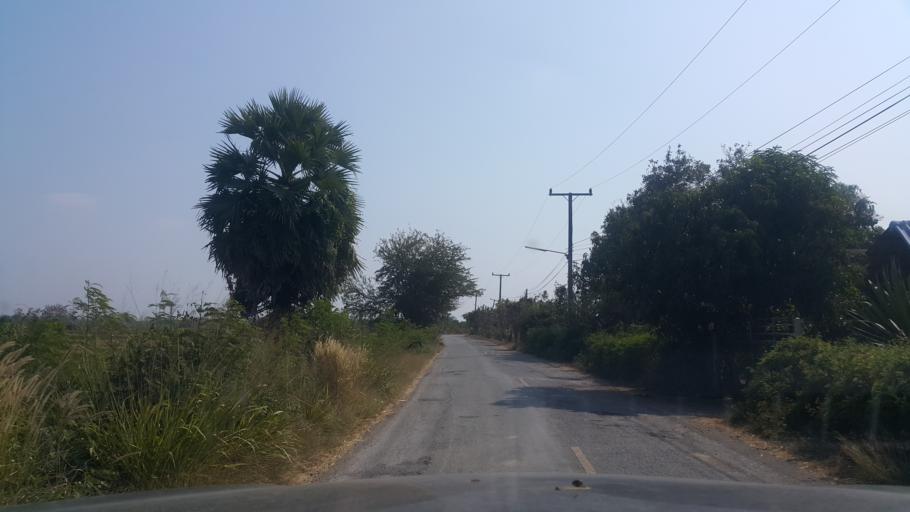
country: TH
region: Nakhon Ratchasima
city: Chok Chai
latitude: 14.7000
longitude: 102.1167
